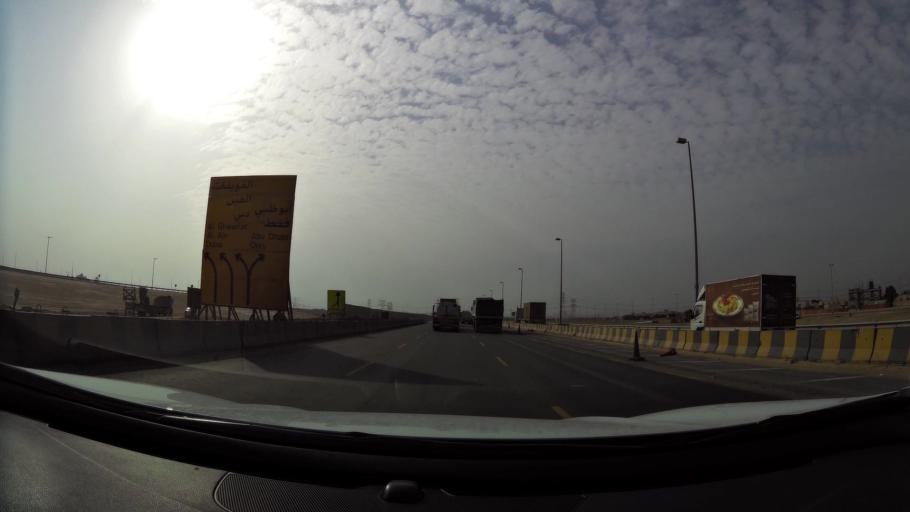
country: AE
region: Abu Dhabi
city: Abu Dhabi
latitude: 24.2925
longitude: 54.5548
